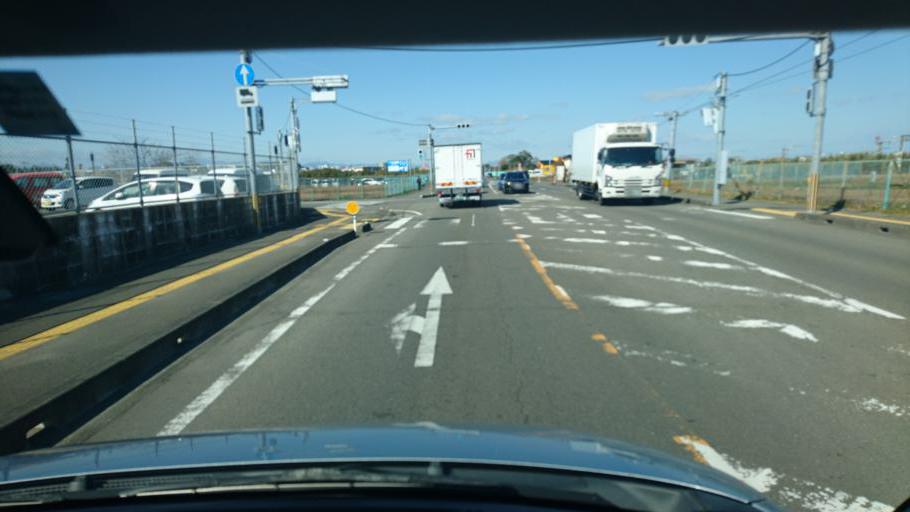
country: JP
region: Miyazaki
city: Miyazaki-shi
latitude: 31.8737
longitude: 131.4311
